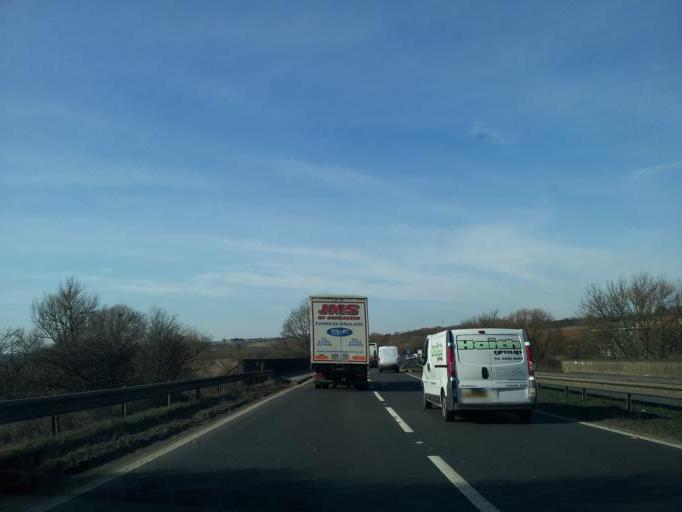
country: GB
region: England
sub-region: Lincolnshire
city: Stamford
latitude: 52.6398
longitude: -0.4948
